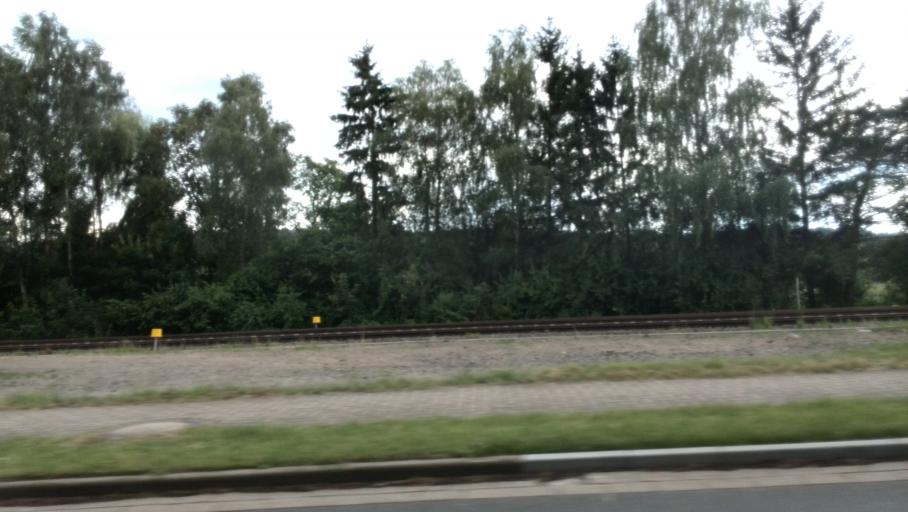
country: DE
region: Lower Saxony
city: Holle
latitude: 52.0984
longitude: 10.1389
